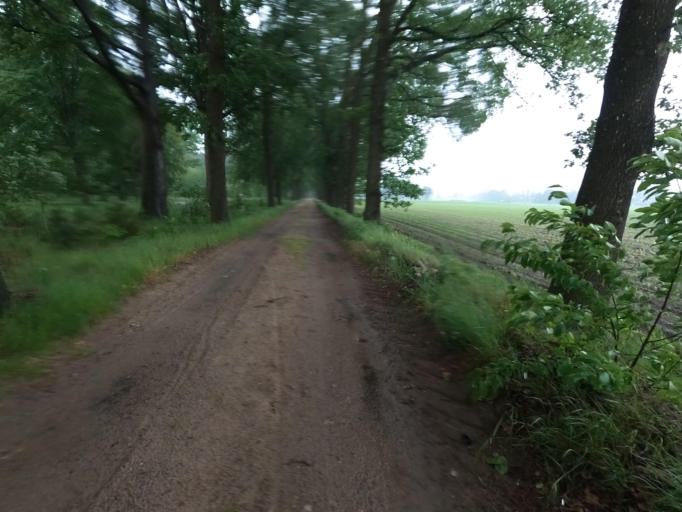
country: BE
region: Flanders
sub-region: Provincie Antwerpen
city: Kalmthout
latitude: 51.4029
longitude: 4.5131
